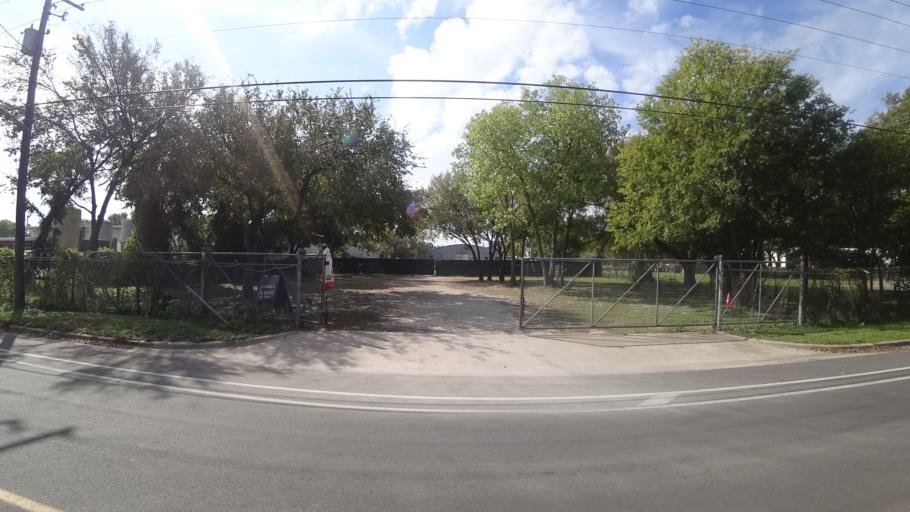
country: US
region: Texas
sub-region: Travis County
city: Austin
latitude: 30.2531
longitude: -97.7010
